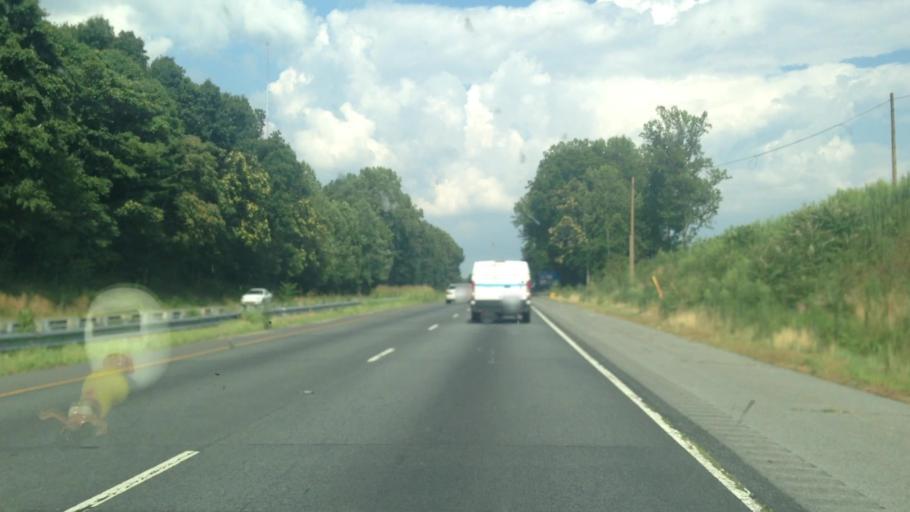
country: US
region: North Carolina
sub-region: Forsyth County
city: Kernersville
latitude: 36.1116
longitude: -80.1092
